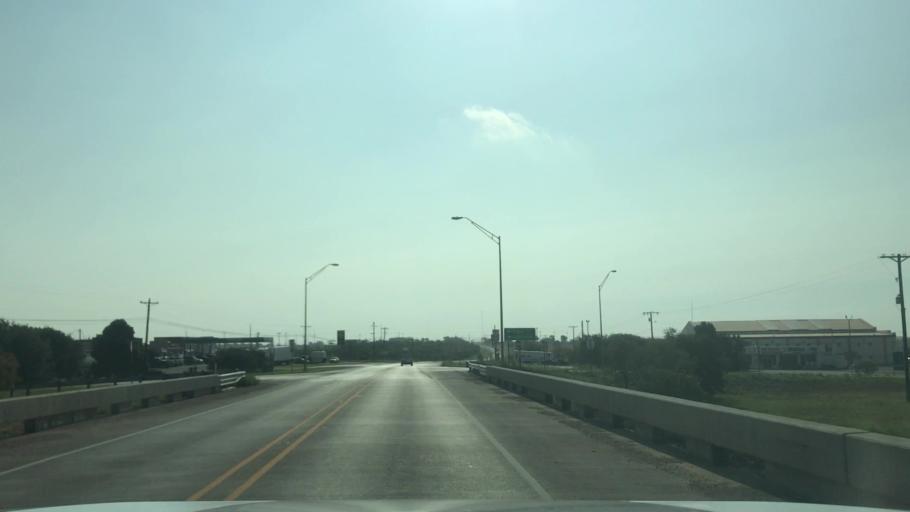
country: US
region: Texas
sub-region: Scurry County
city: Snyder
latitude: 32.7046
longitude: -100.8682
